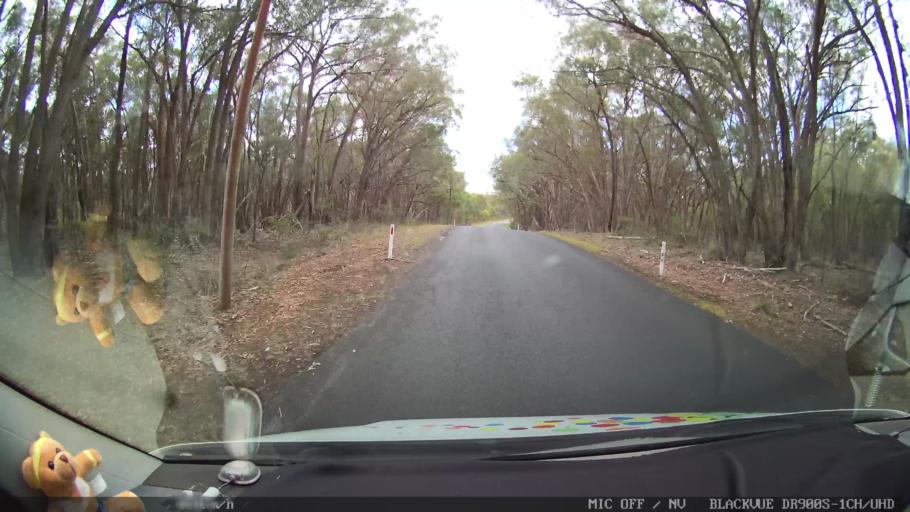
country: AU
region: New South Wales
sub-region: Glen Innes Severn
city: Glen Innes
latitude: -29.4320
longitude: 151.6352
